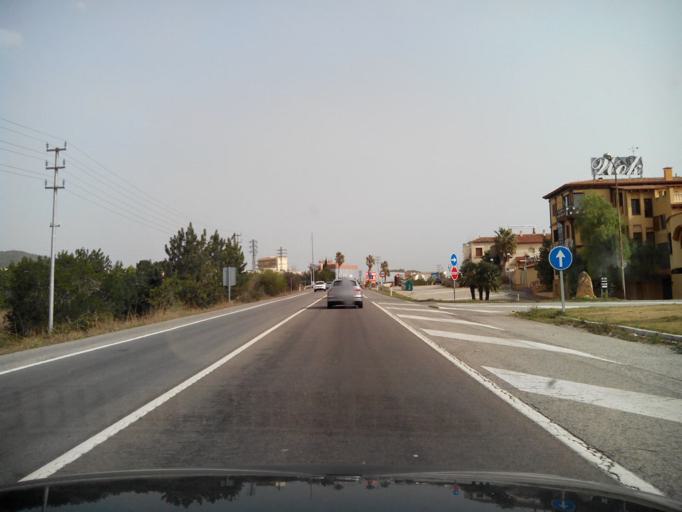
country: ES
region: Catalonia
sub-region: Provincia de Tarragona
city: Roda de Bara
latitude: 41.1753
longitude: 1.4725
